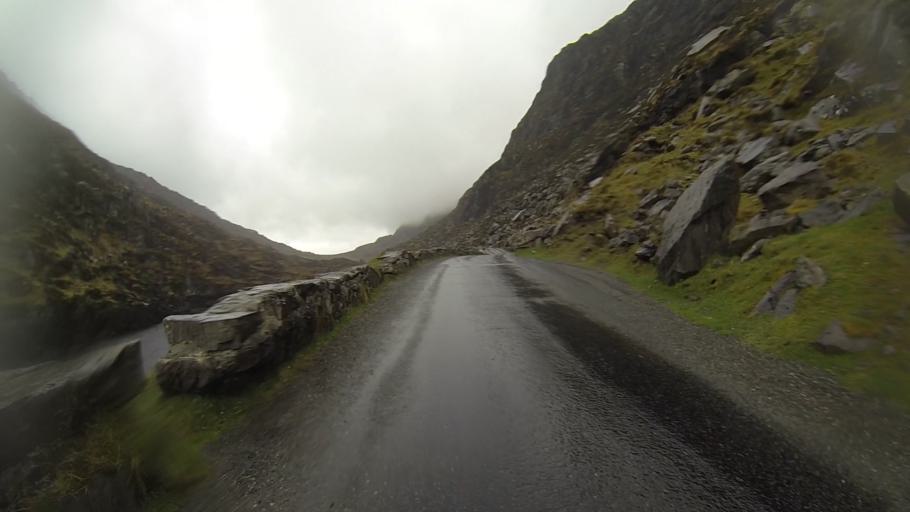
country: IE
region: Munster
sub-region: Ciarrai
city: Cill Airne
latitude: 52.0065
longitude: -9.6425
